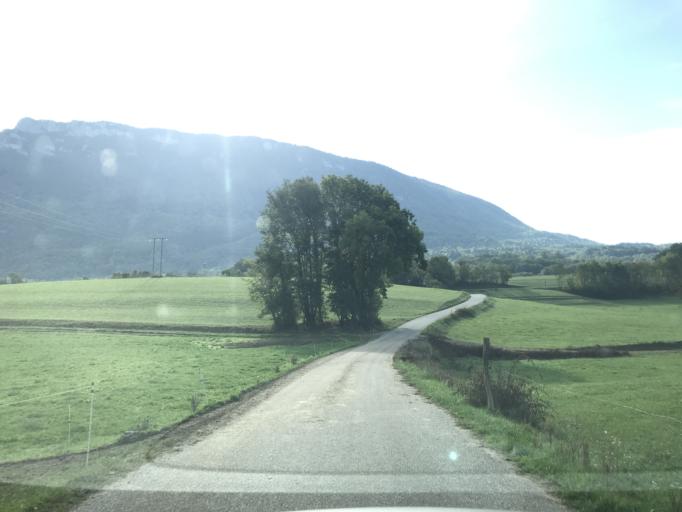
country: FR
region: Rhone-Alpes
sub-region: Departement de la Savoie
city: Yenne
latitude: 45.6870
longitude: 5.7952
